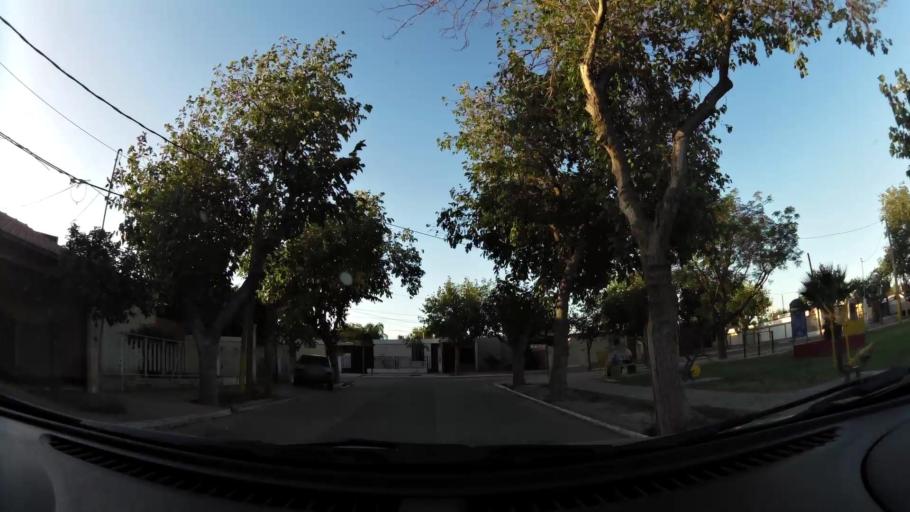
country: AR
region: San Juan
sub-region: Departamento de Santa Lucia
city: Santa Lucia
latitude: -31.5271
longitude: -68.5070
